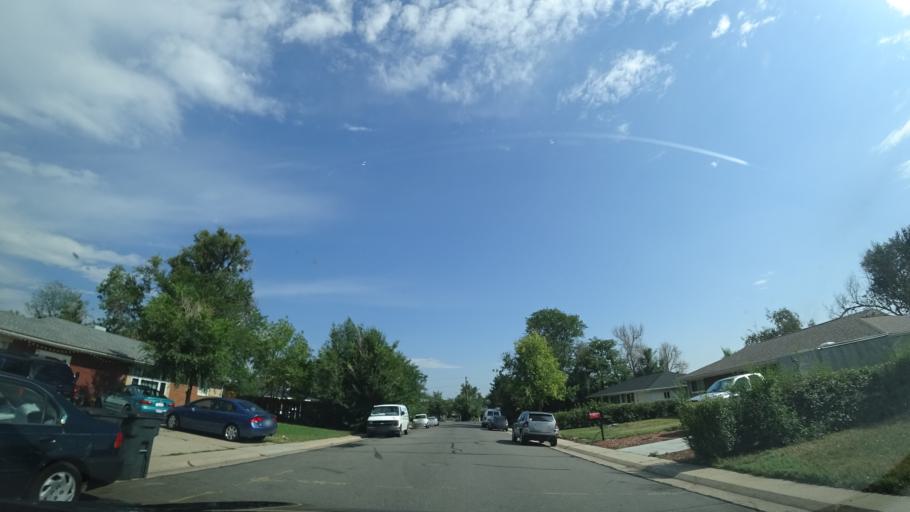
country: US
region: Colorado
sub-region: Jefferson County
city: Lakewood
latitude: 39.7176
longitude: -105.0569
